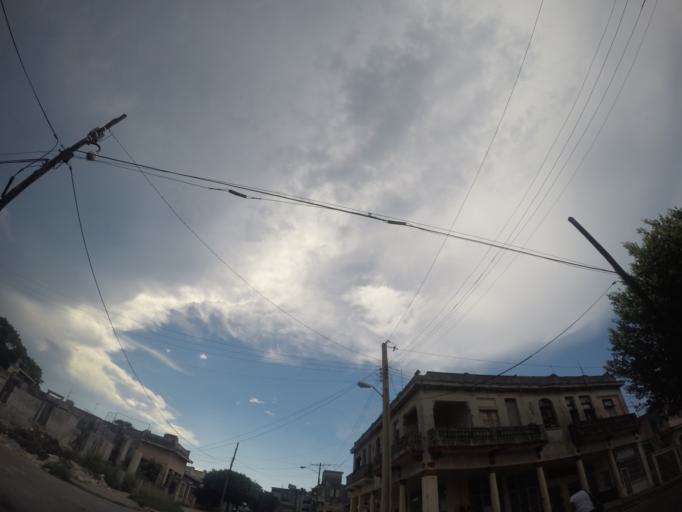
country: CU
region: La Habana
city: Havana
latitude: 23.1165
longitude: -82.4215
